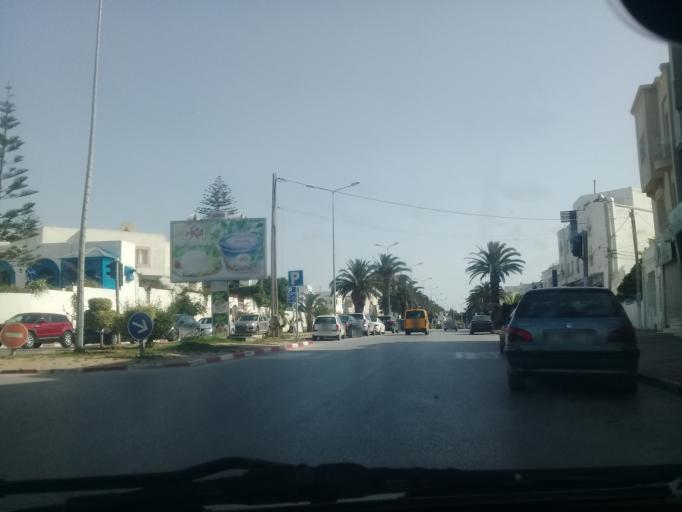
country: TN
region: Tunis
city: Al Marsa
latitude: 36.8794
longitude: 10.3275
